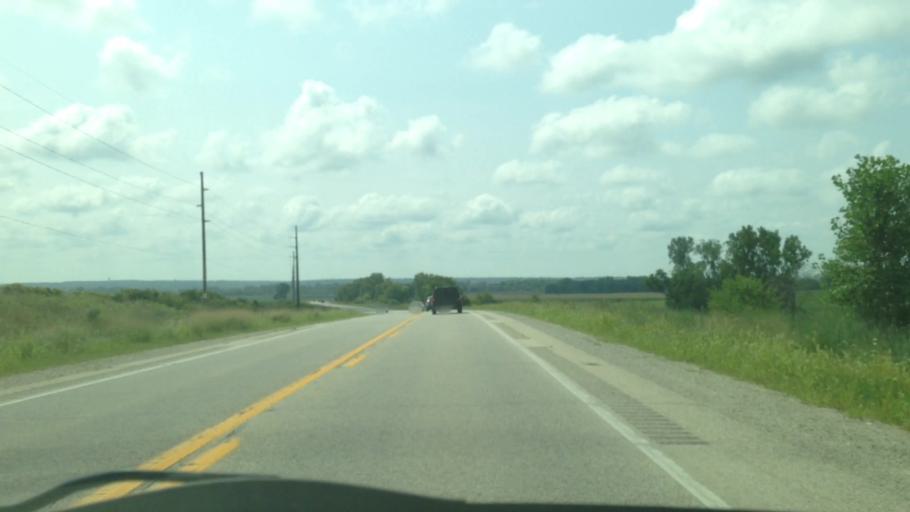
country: US
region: Iowa
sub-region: Benton County
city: Walford
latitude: 41.8227
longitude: -91.8731
